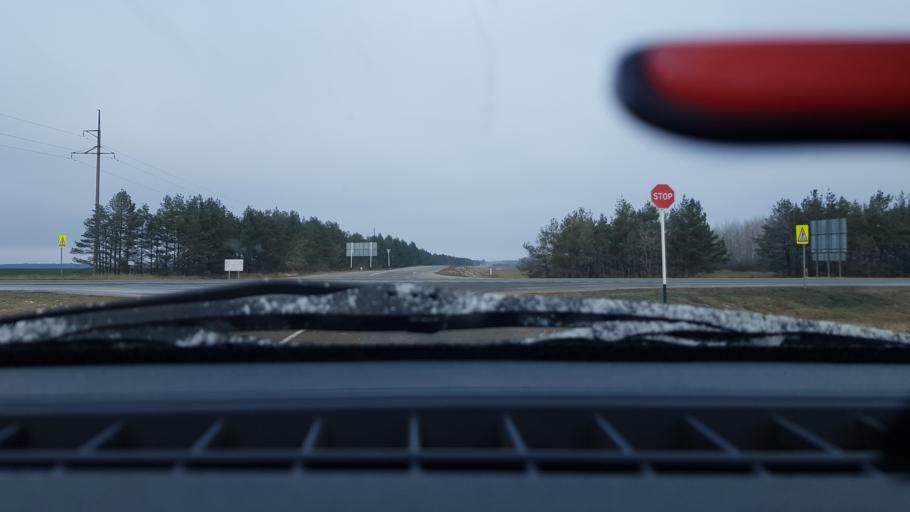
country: RU
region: Tatarstan
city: Kuybyshevskiy Zaton
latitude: 54.9465
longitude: 49.4502
